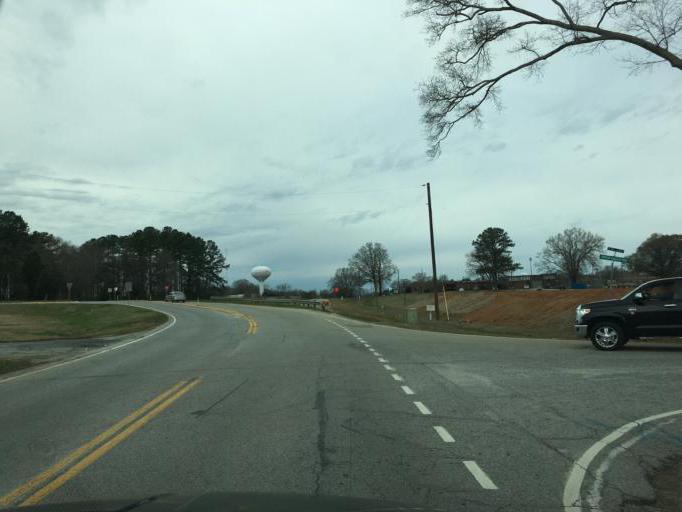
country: US
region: South Carolina
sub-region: Pickens County
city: Clemson
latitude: 34.6757
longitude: -82.8148
